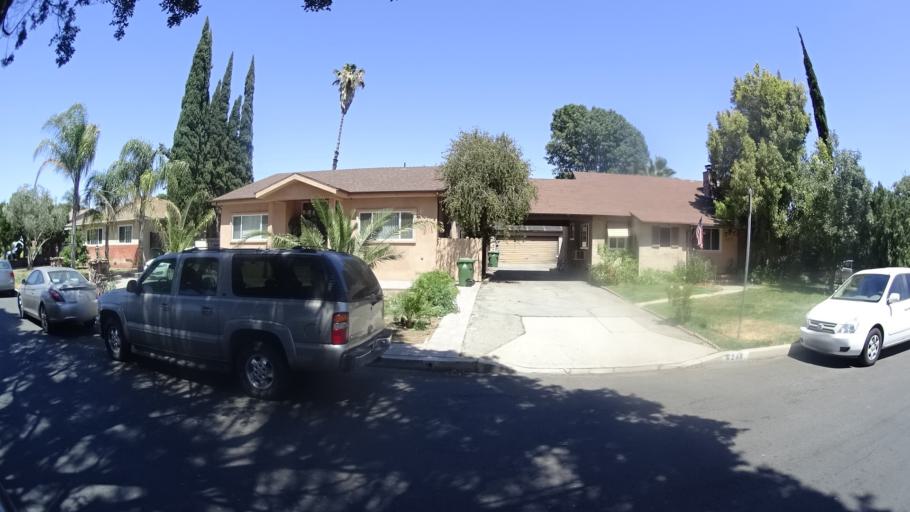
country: US
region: California
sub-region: Los Angeles County
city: Van Nuys
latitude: 34.1847
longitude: -118.4685
